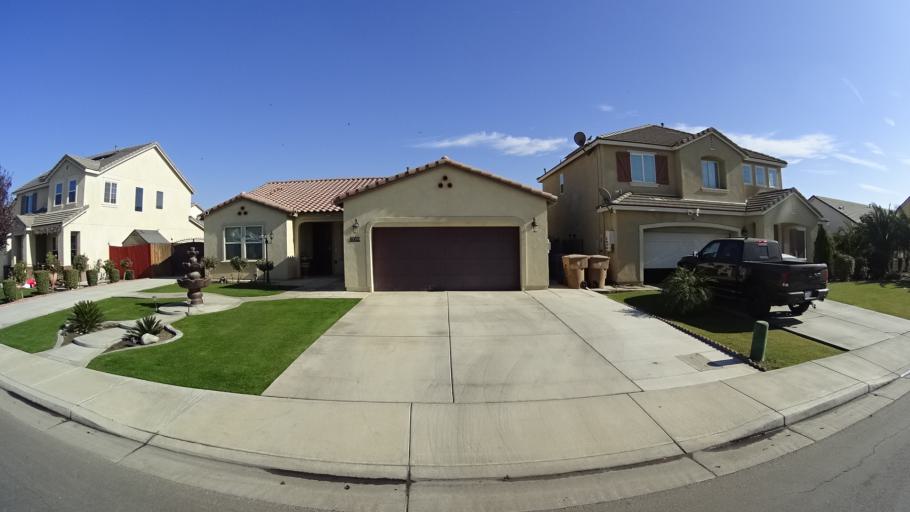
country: US
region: California
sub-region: Kern County
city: Greenfield
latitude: 35.2827
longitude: -119.0587
